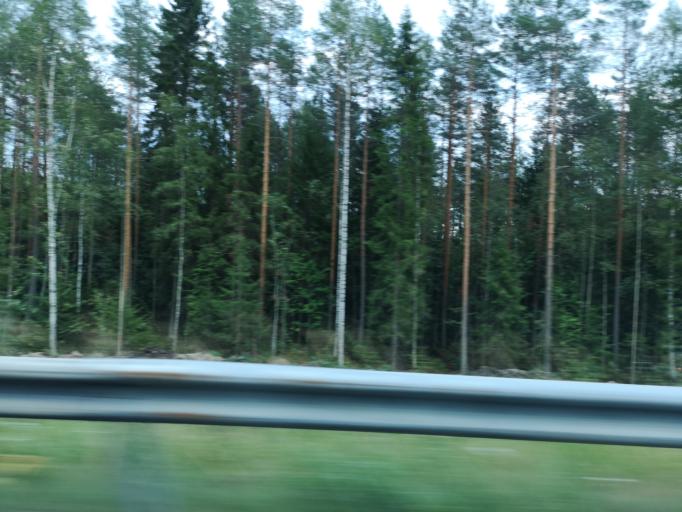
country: FI
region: Central Finland
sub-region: Joutsa
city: Leivonmaeki
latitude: 61.8426
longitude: 26.0984
